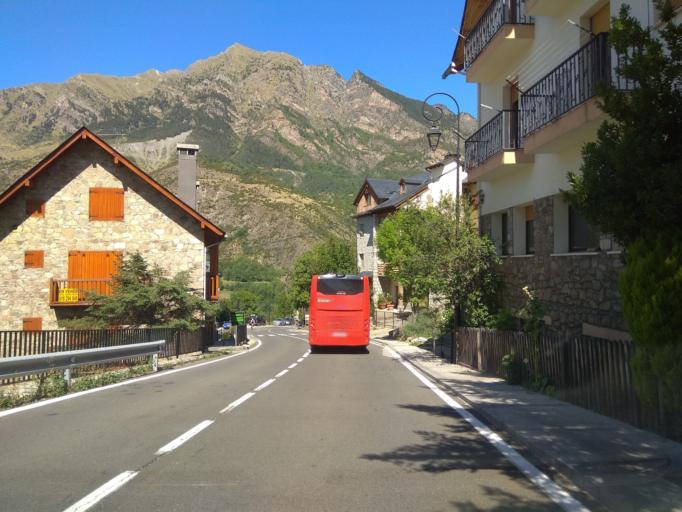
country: ES
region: Catalonia
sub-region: Provincia de Lleida
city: Vielha
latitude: 42.5217
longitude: 0.8351
